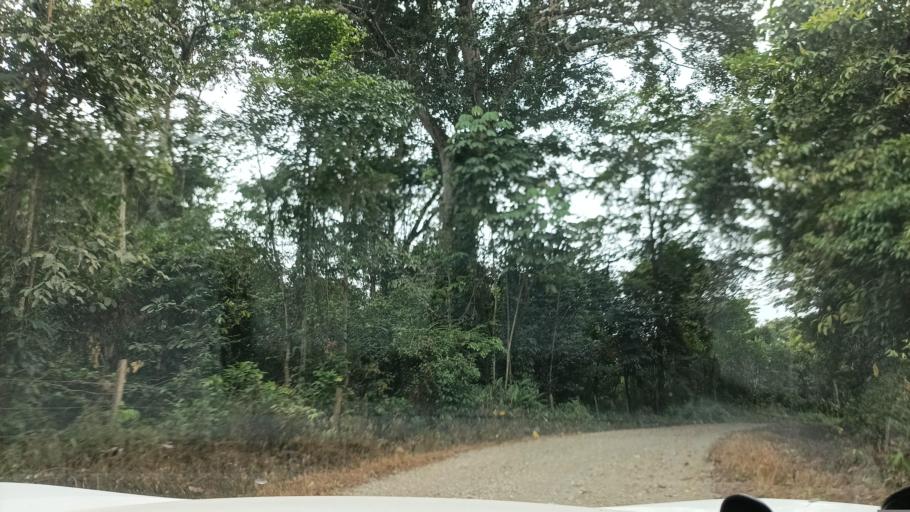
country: MX
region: Veracruz
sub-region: Uxpanapa
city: Poblado 10
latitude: 17.4391
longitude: -94.4103
